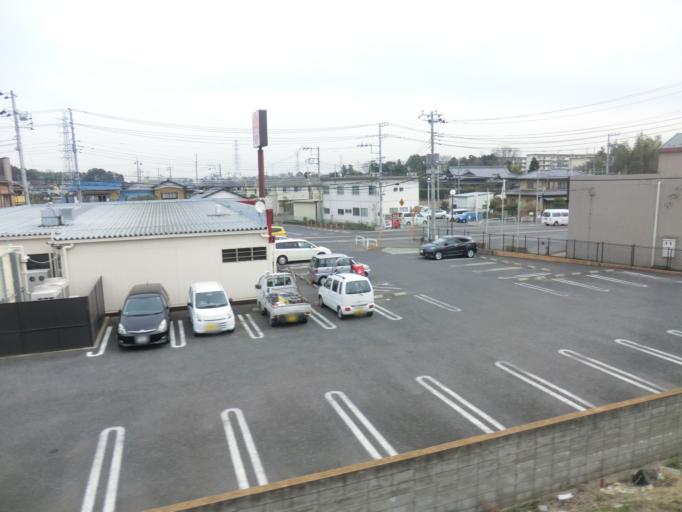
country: JP
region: Chiba
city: Kashiwa
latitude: 35.8623
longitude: 139.9515
